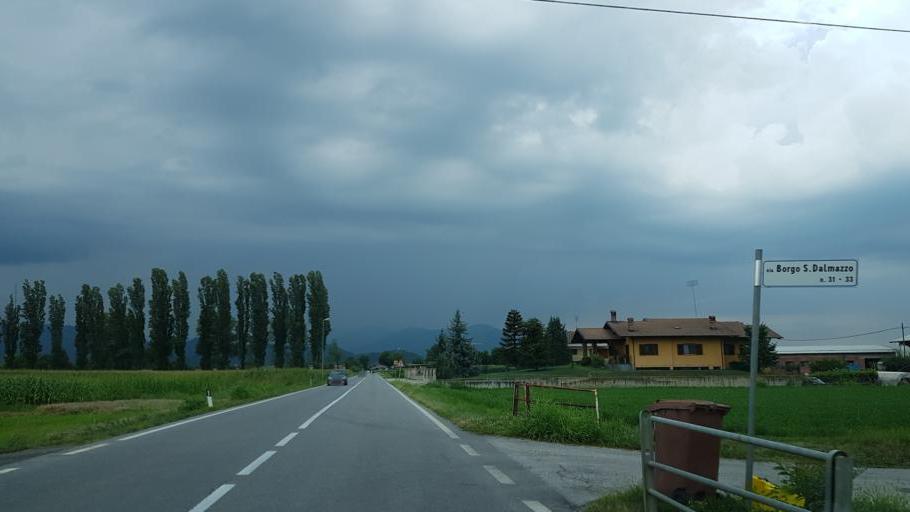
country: IT
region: Piedmont
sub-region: Provincia di Cuneo
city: San Rocco
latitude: 44.3952
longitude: 7.4546
